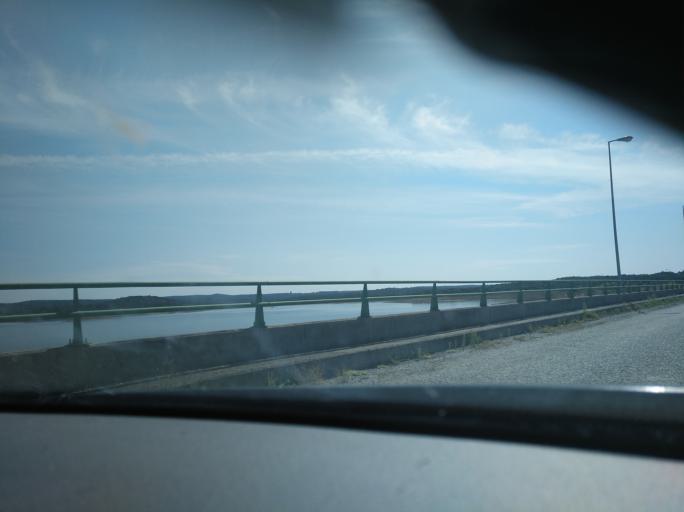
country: PT
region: Evora
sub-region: Montemor-O-Novo
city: Montemor-o-Novo
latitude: 38.6583
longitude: -8.0981
